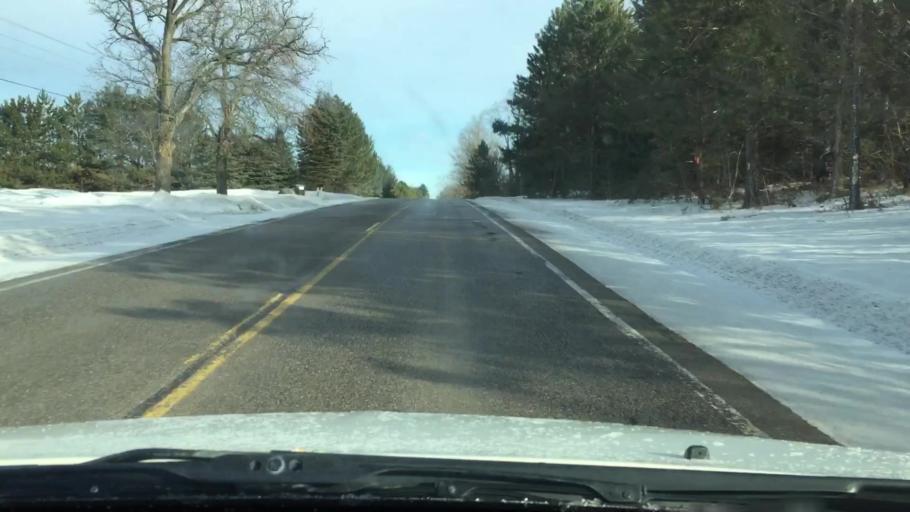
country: US
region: Michigan
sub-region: Kalkaska County
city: Kalkaska
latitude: 44.6408
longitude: -85.2429
